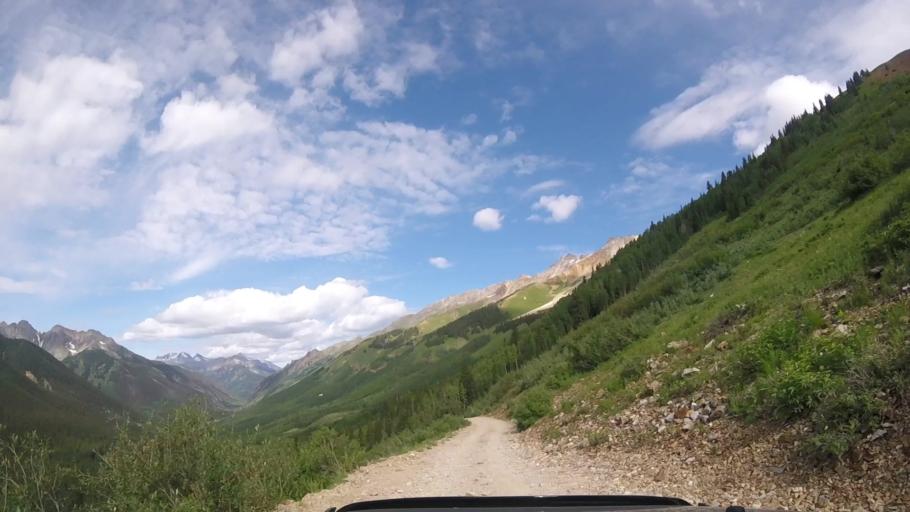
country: US
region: Colorado
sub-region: San Miguel County
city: Telluride
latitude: 37.8585
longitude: -107.7924
